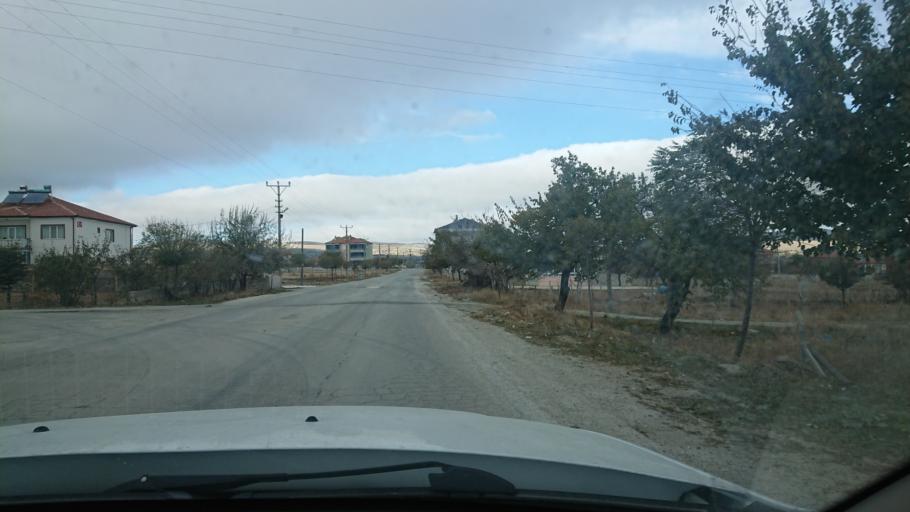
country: TR
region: Aksaray
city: Ortakoy
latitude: 38.7440
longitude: 34.0315
